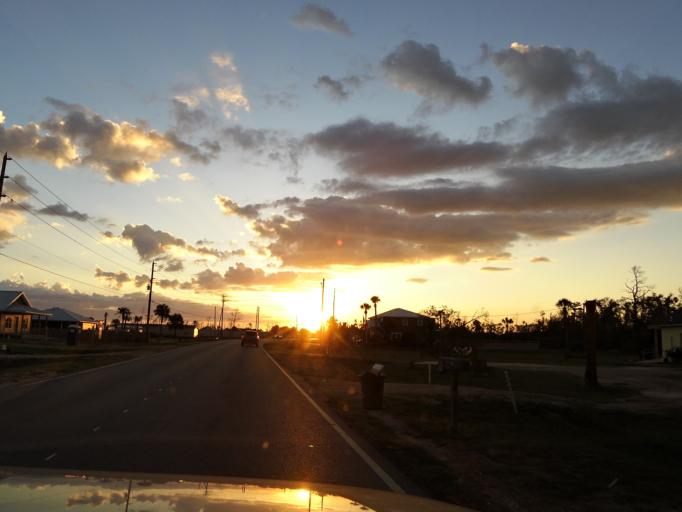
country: US
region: Florida
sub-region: Bay County
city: Mexico Beach
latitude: 29.9408
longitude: -85.3894
